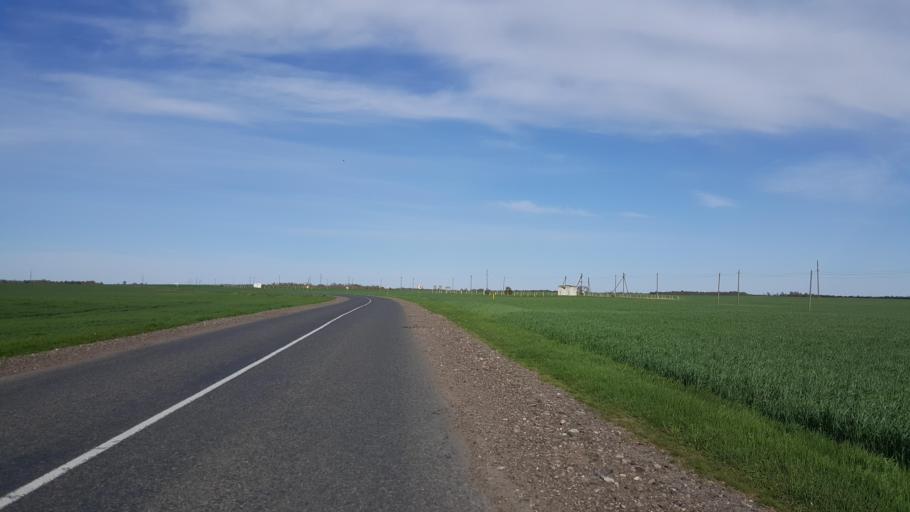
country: BY
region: Brest
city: Vysokaye
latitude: 52.3870
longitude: 23.4545
